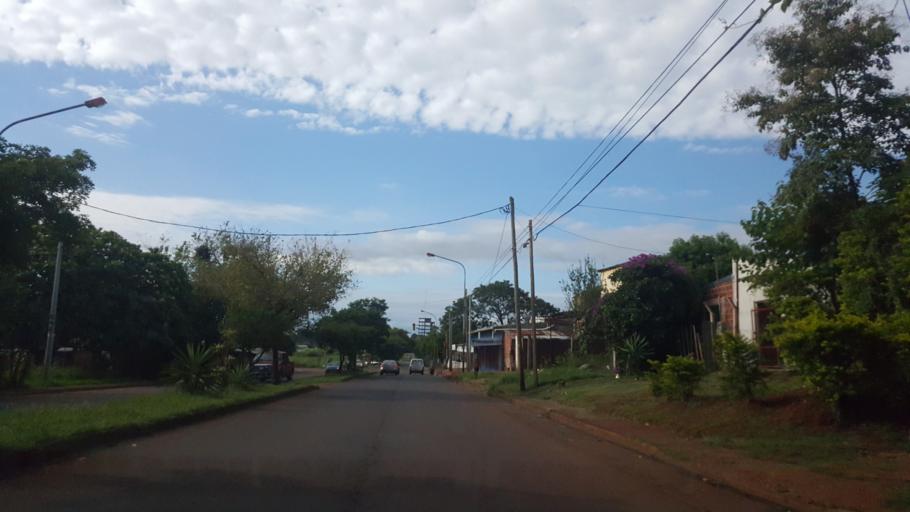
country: AR
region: Misiones
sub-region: Departamento de Capital
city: Posadas
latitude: -27.3782
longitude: -55.9332
